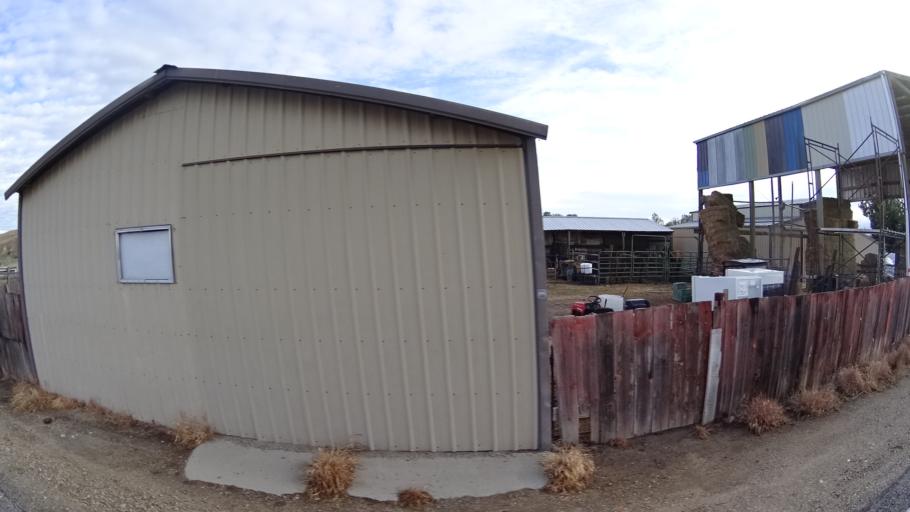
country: US
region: Idaho
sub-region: Ada County
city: Star
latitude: 43.7718
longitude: -116.4919
